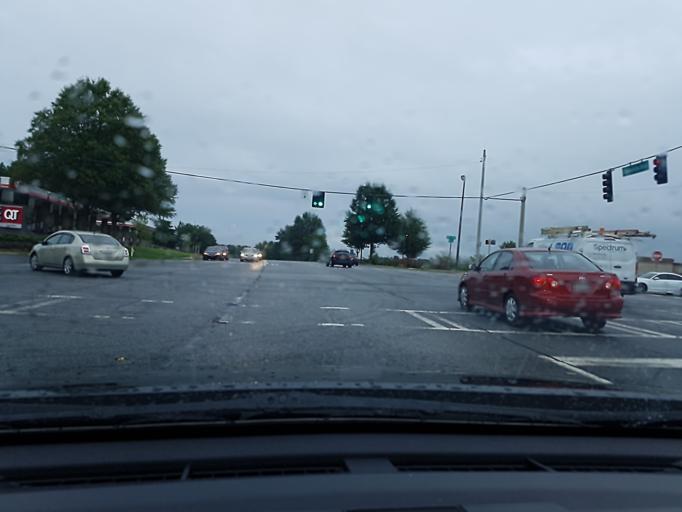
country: US
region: Georgia
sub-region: Gwinnett County
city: Duluth
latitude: 33.9697
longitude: -84.0980
